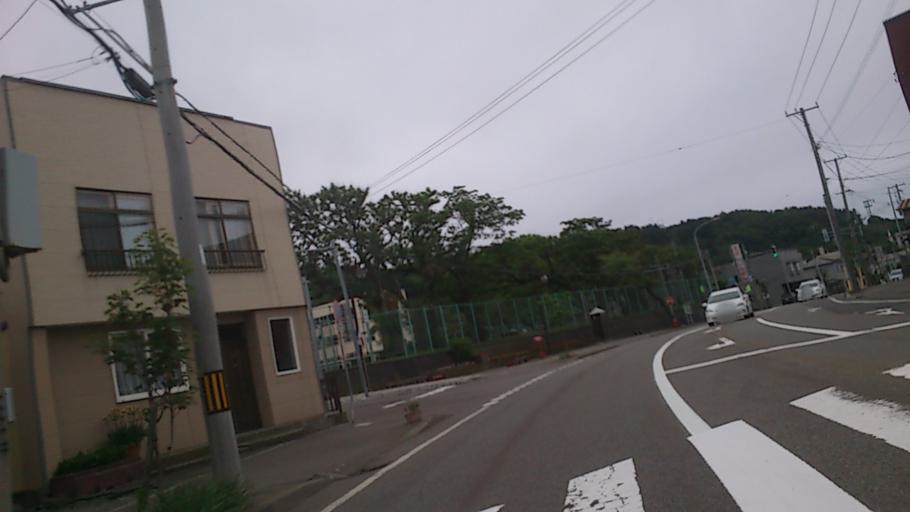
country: JP
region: Hokkaido
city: Kamiiso
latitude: 41.9701
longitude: 140.1378
